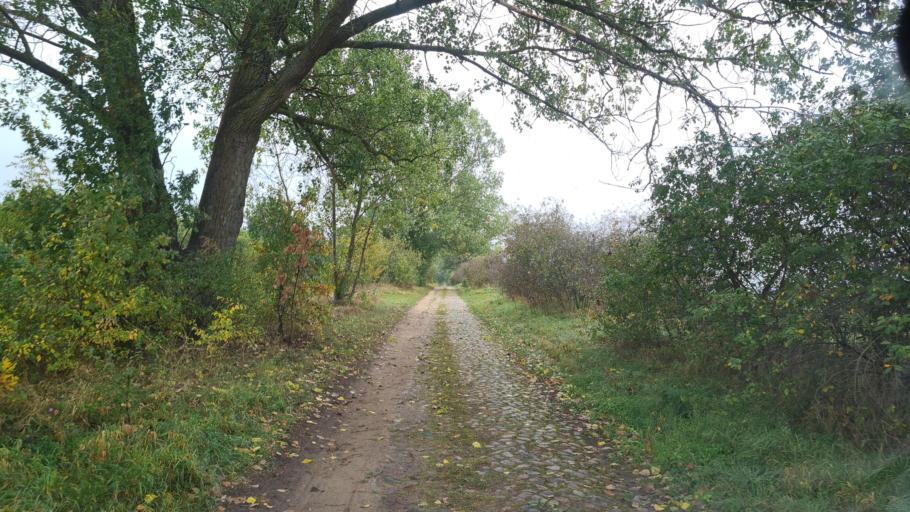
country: DE
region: Brandenburg
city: Furstenwalde
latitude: 52.4287
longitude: 14.0199
